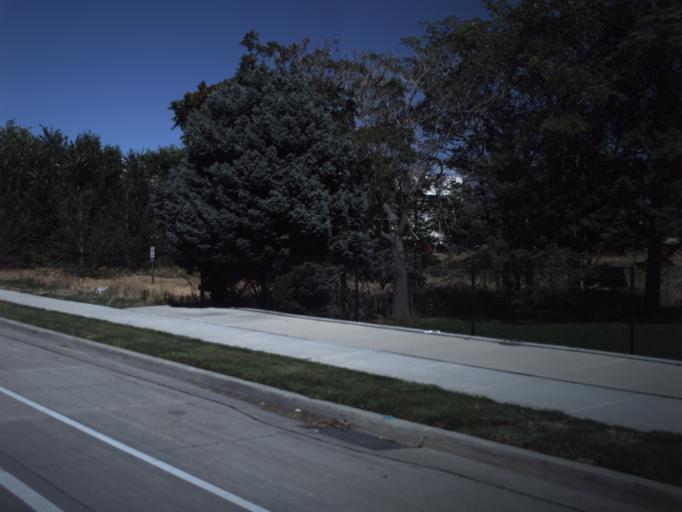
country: US
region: Utah
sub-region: Salt Lake County
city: Riverton
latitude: 40.5409
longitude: -111.9386
